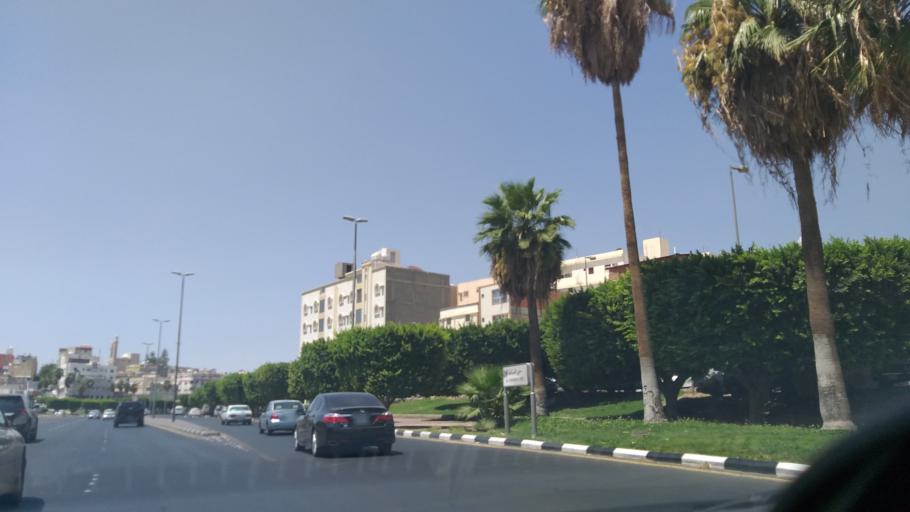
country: SA
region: Makkah
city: Ta'if
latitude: 21.2743
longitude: 40.4212
